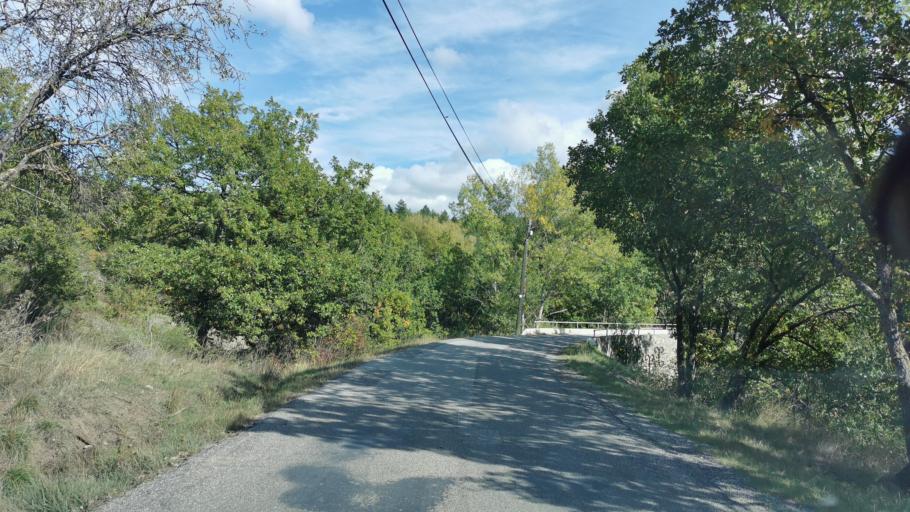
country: FR
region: Provence-Alpes-Cote d'Azur
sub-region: Departement des Alpes-de-Haute-Provence
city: Sisteron
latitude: 44.1874
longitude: 6.0039
